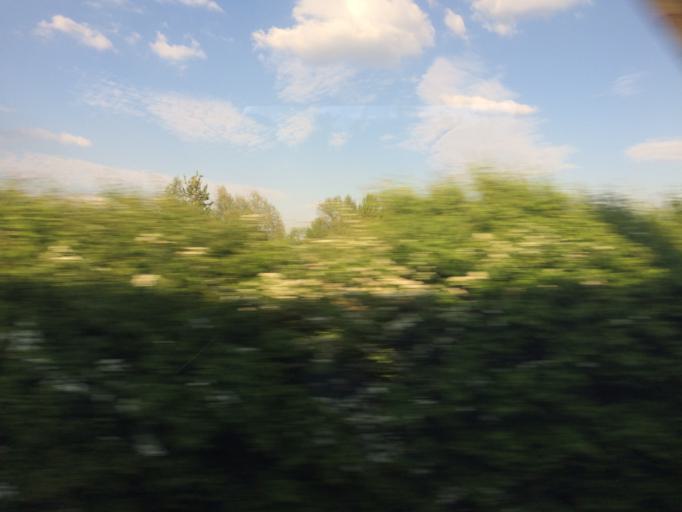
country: DE
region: North Rhine-Westphalia
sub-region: Regierungsbezirk Dusseldorf
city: Ratingen
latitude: 51.3151
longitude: 6.7841
